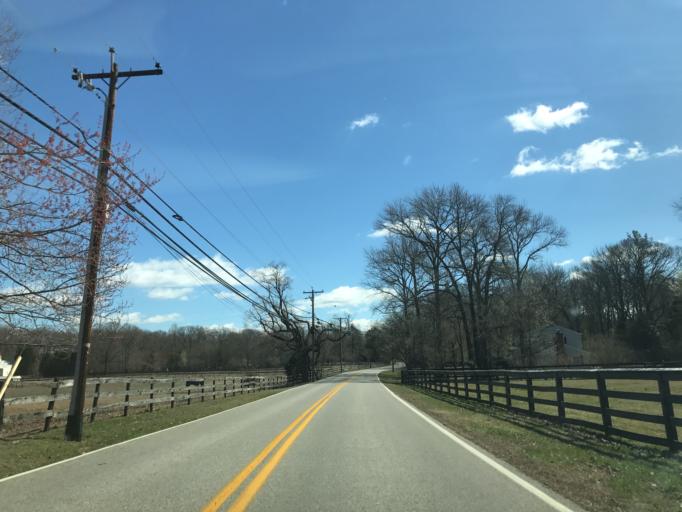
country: US
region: Maryland
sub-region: Anne Arundel County
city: Robinwood
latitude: 38.9533
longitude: -76.5202
